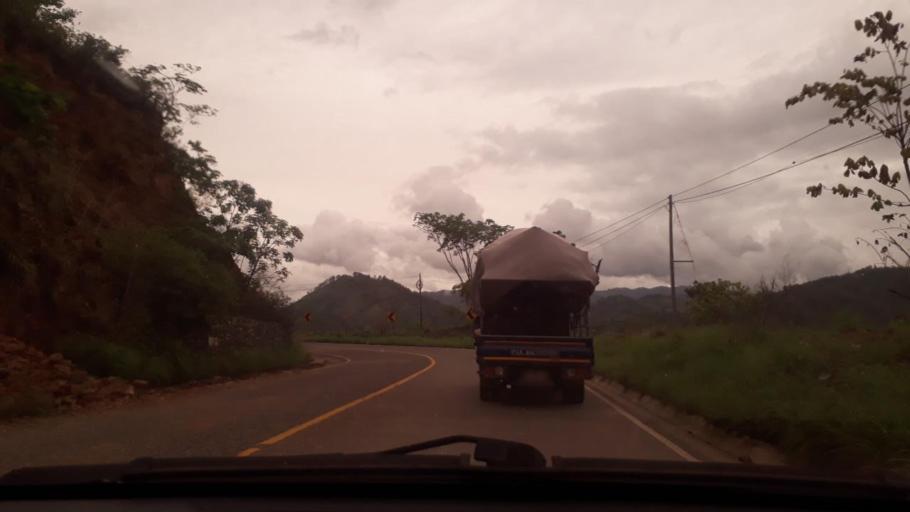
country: GT
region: Chiquimula
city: San Jose La Arada
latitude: 14.7189
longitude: -89.5908
